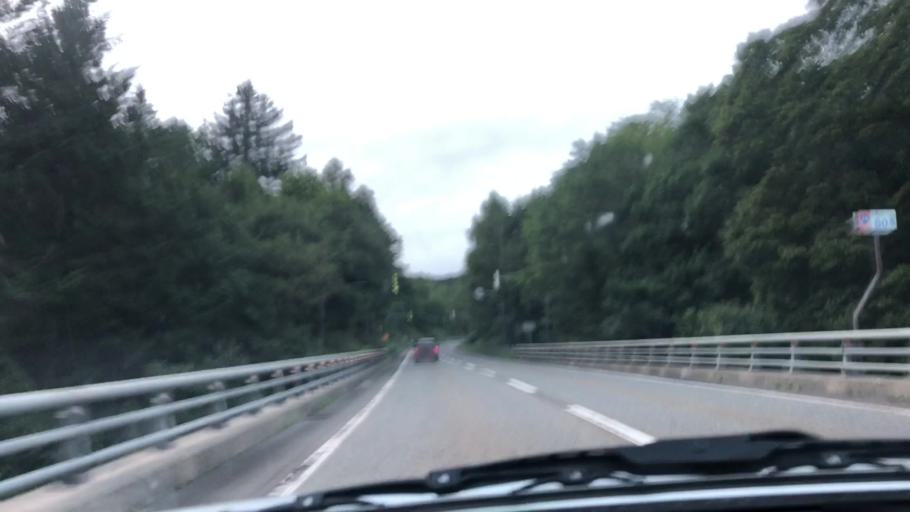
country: JP
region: Hokkaido
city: Iwamizawa
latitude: 42.9039
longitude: 142.1275
